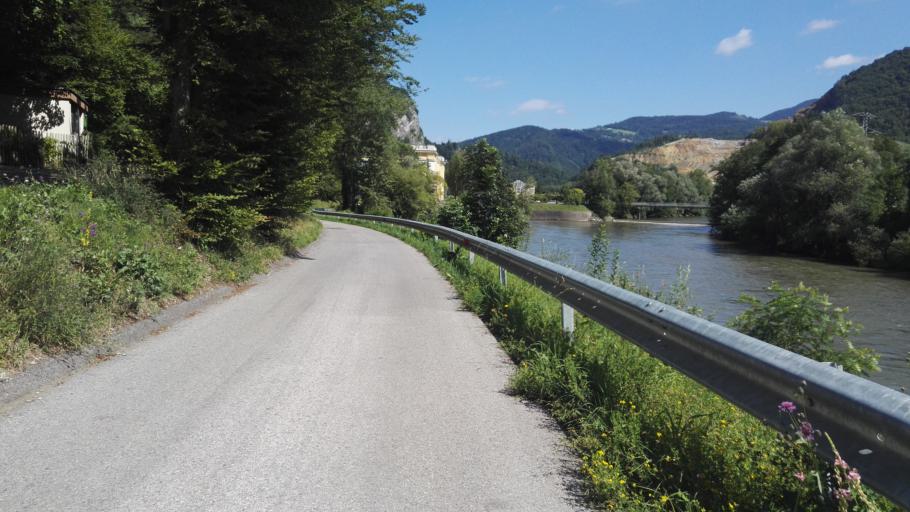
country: AT
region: Styria
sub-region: Politischer Bezirk Graz-Umgebung
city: Peggau
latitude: 47.2065
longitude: 15.3362
